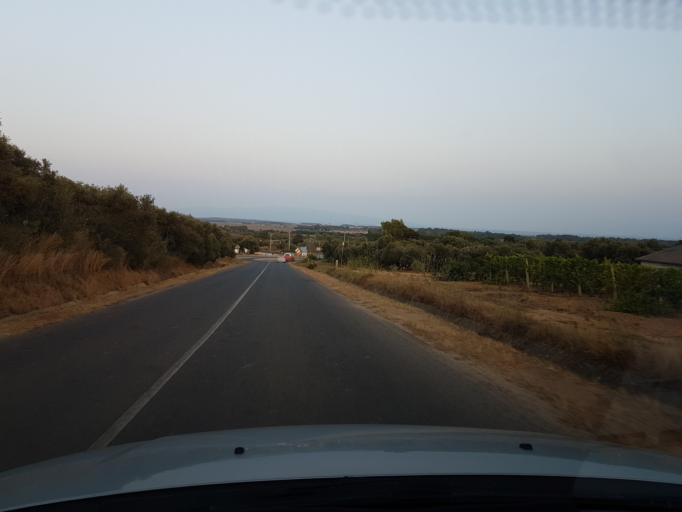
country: IT
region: Sardinia
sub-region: Provincia di Oristano
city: Cabras
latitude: 39.9298
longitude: 8.4542
